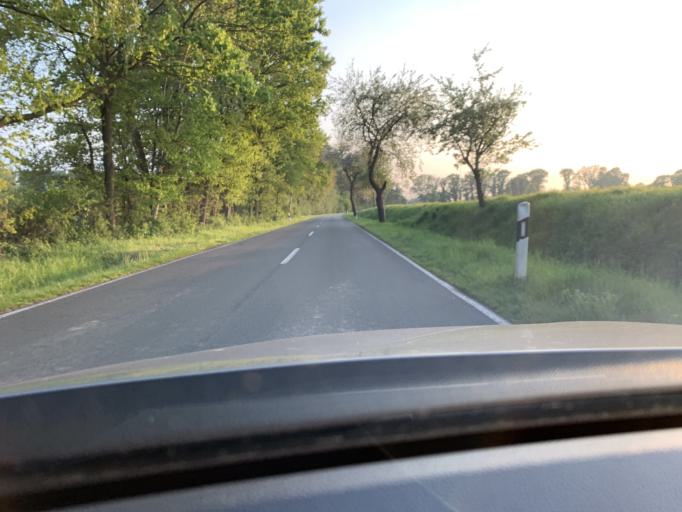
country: DE
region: North Rhine-Westphalia
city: Rietberg
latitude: 51.7808
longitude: 8.4013
